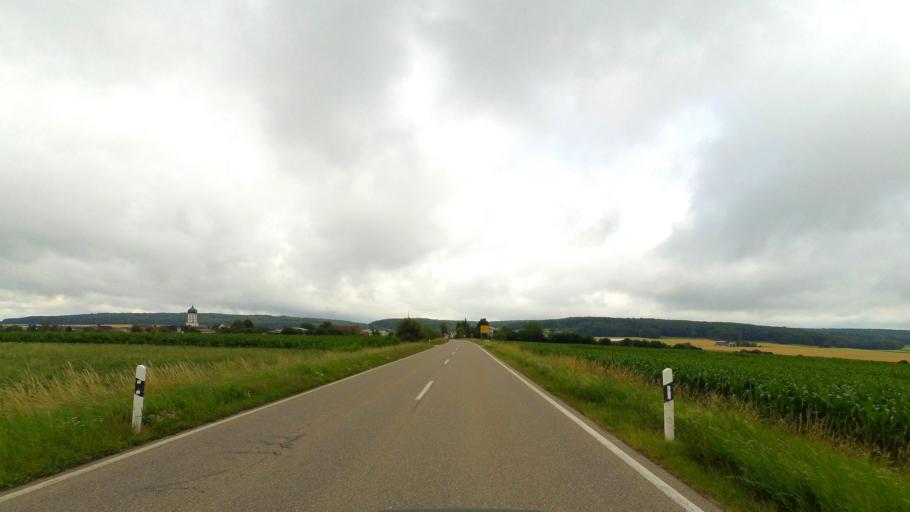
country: DE
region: Baden-Wuerttemberg
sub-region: Tuebingen Region
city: Weidenstetten
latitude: 48.5537
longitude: 10.0047
